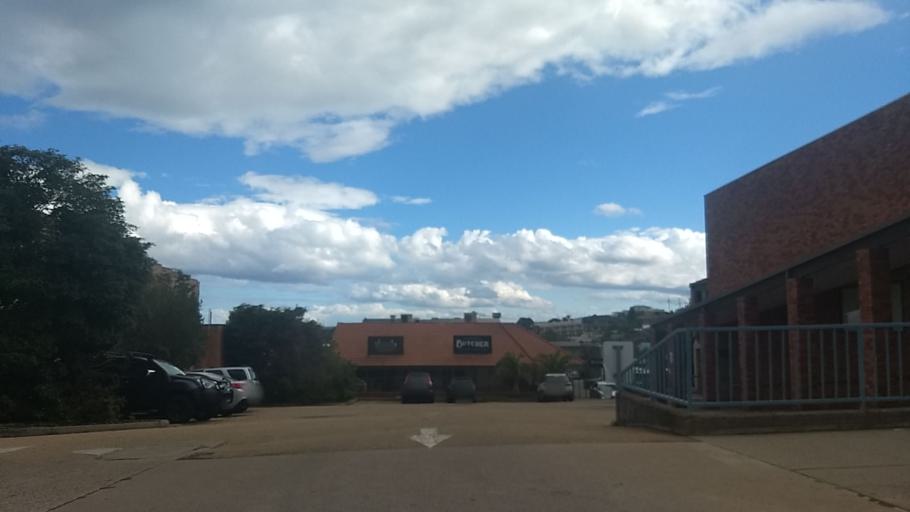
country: AU
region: New South Wales
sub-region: Bega Valley
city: Merimbula
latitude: -36.8869
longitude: 149.9096
